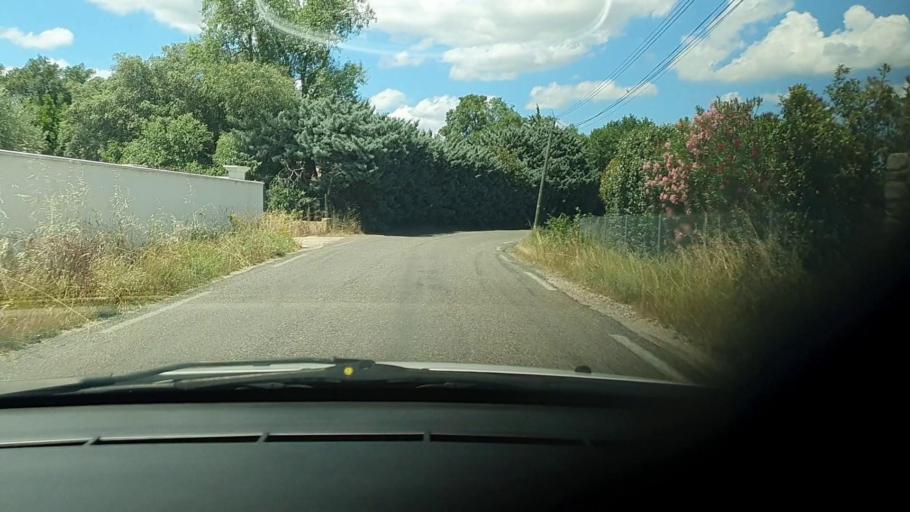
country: FR
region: Languedoc-Roussillon
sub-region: Departement du Gard
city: Montaren-et-Saint-Mediers
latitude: 44.0073
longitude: 4.3888
